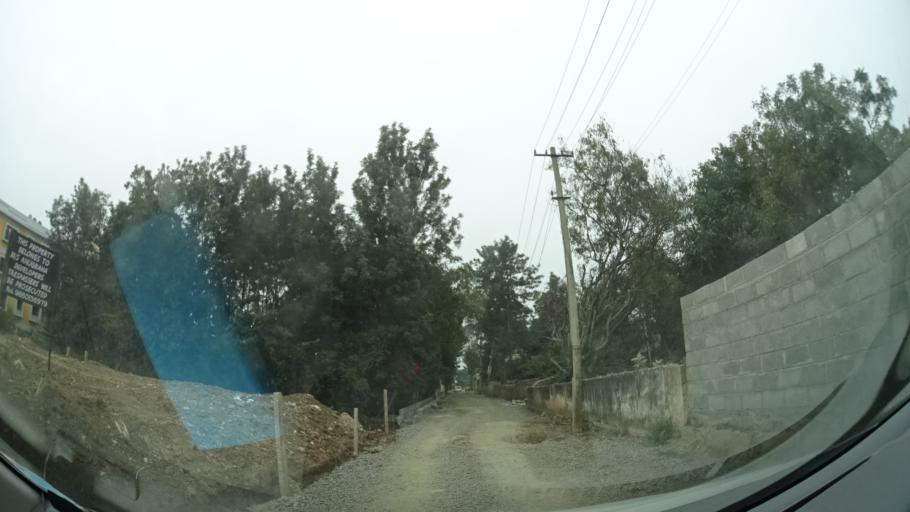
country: IN
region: Karnataka
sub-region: Bangalore Rural
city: Hoskote
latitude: 12.9780
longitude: 77.7434
